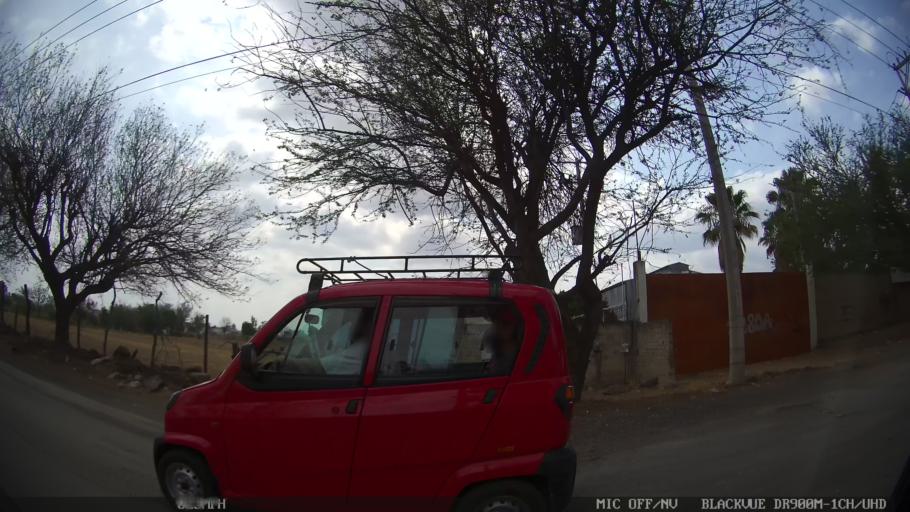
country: MX
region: Jalisco
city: Tonala
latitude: 20.6358
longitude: -103.2209
